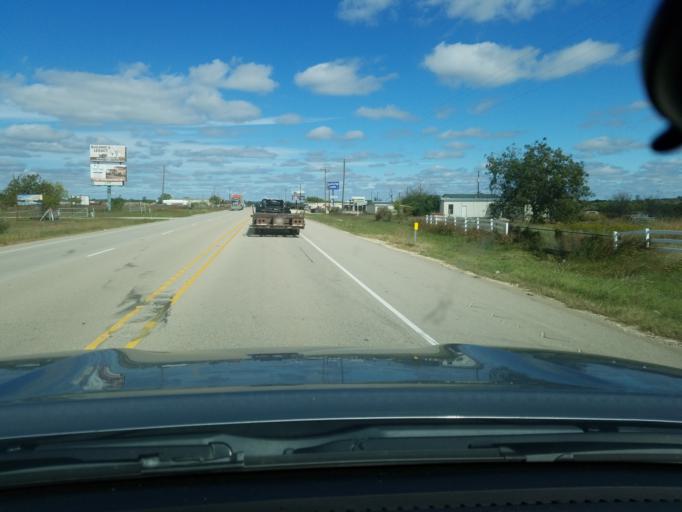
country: US
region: Texas
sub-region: Hamilton County
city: Hamilton
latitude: 31.6751
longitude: -98.1357
